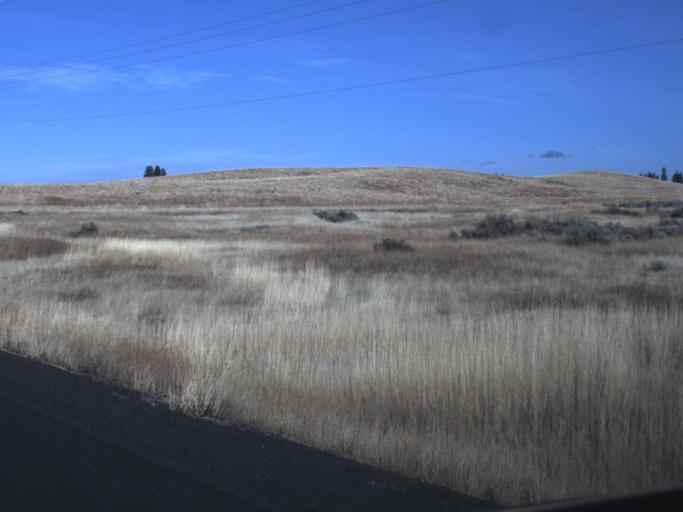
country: US
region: Washington
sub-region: Lincoln County
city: Davenport
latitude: 47.7474
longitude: -118.1716
